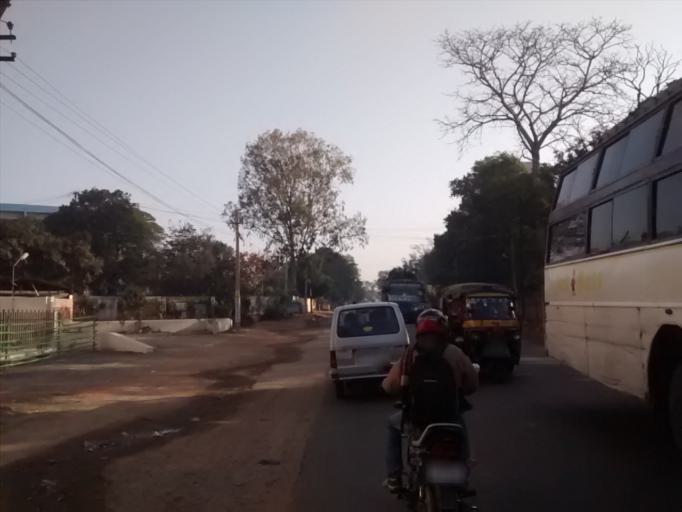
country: IN
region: Jharkhand
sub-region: Ranchi
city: Ranchi
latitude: 23.3830
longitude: 85.3675
